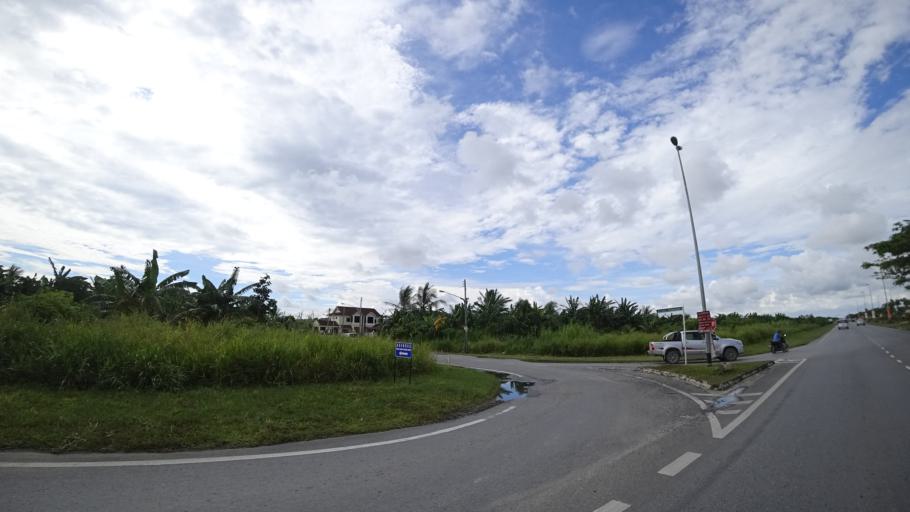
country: MY
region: Sarawak
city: Miri
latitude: 4.4664
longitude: 114.0419
